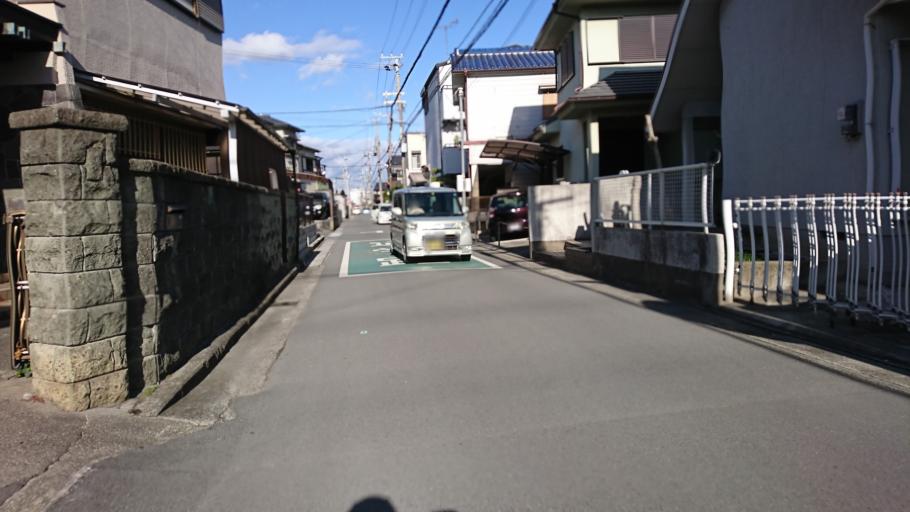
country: JP
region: Hyogo
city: Kakogawacho-honmachi
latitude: 34.7709
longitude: 134.7744
